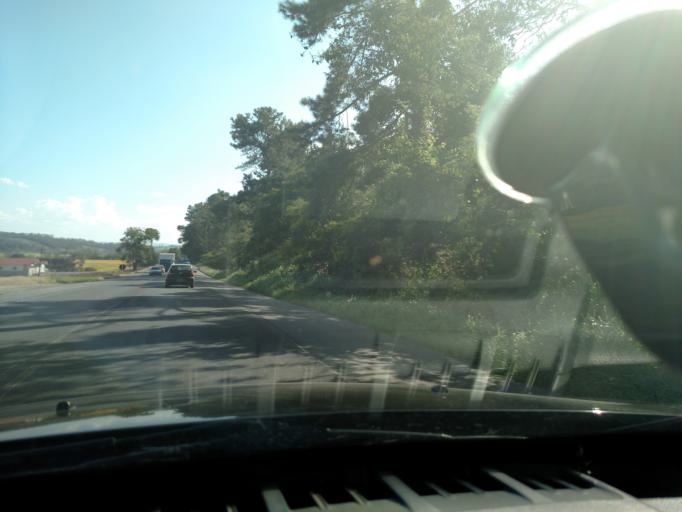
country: BR
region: Santa Catarina
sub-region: Rio Do Sul
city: Rio do Sul
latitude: -27.2673
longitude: -49.7286
